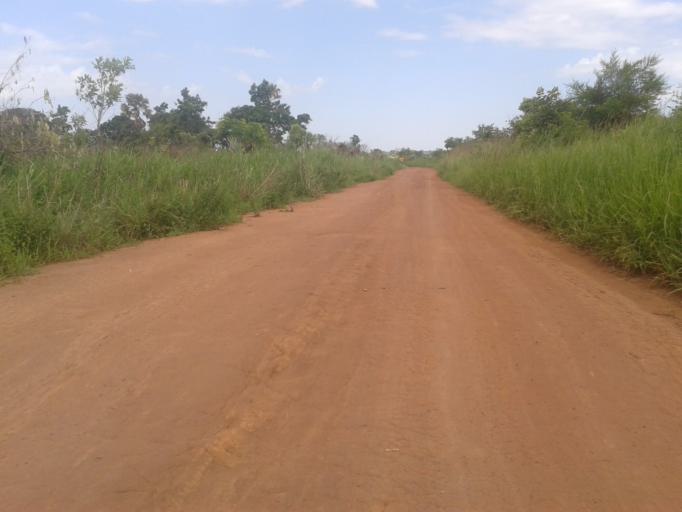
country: UG
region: Northern Region
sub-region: Gulu District
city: Gulu
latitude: 2.8280
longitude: 32.2381
